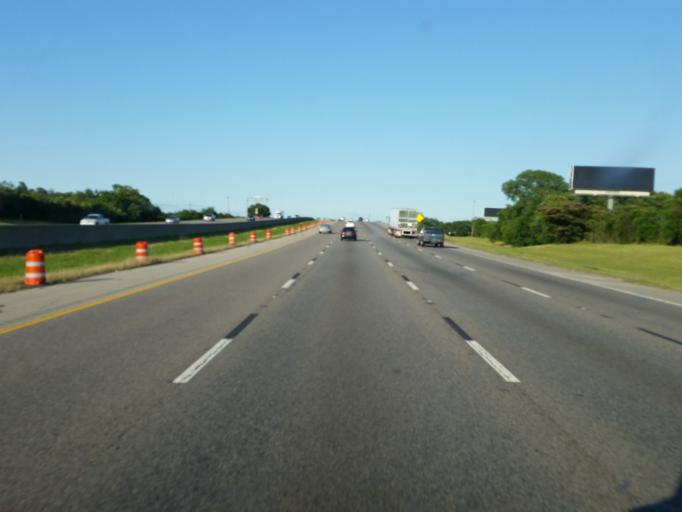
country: US
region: Texas
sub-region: Dallas County
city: Balch Springs
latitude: 32.6855
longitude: -96.6443
